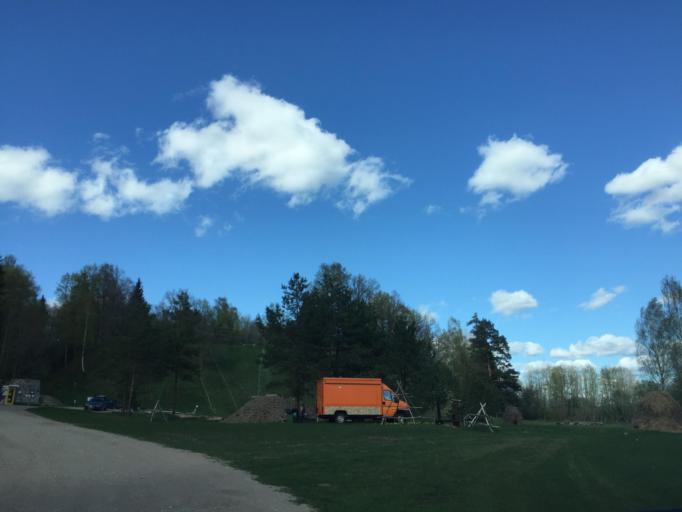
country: LV
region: Madonas Rajons
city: Madona
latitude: 56.8092
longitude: 26.0947
